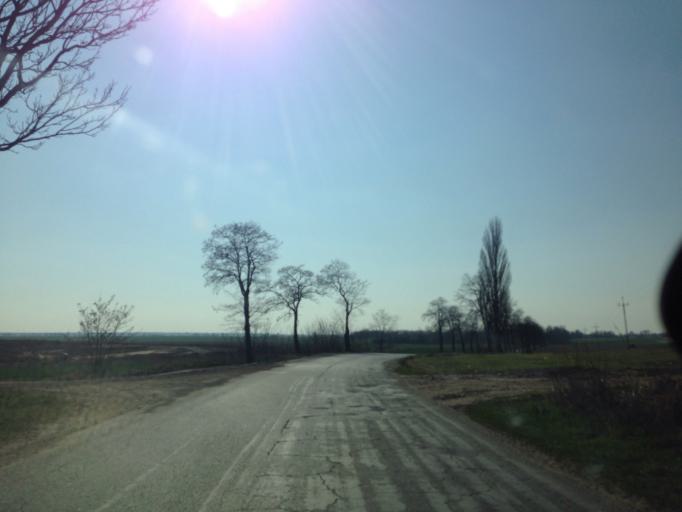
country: PL
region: Lower Silesian Voivodeship
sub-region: Powiat olesnicki
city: Bierutow
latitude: 51.1945
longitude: 17.5285
